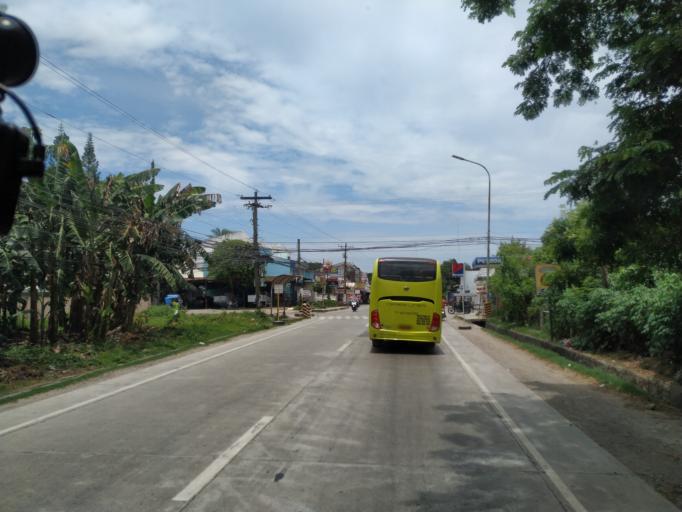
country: PH
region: Central Visayas
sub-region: Province of Negros Oriental
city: Sibulan
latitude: 9.3562
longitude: 123.2846
